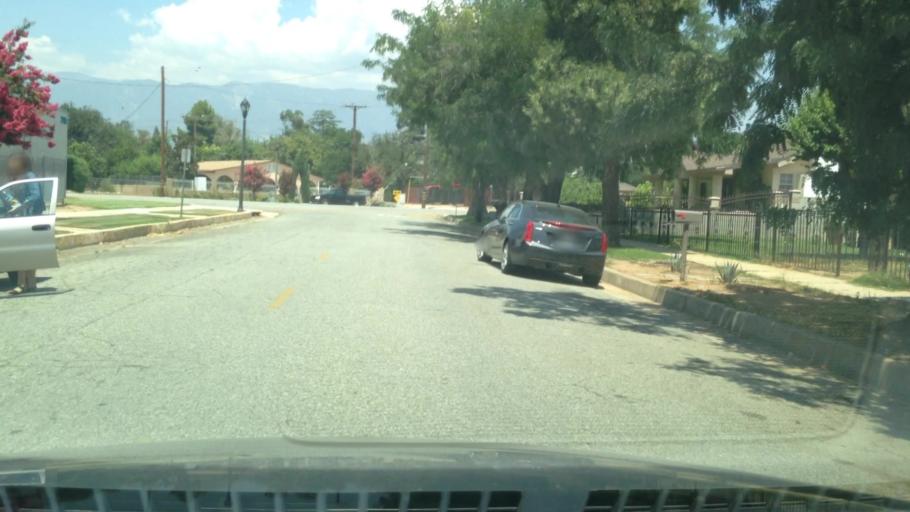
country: US
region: California
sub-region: Riverside County
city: Beaumont
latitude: 33.9319
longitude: -116.9827
